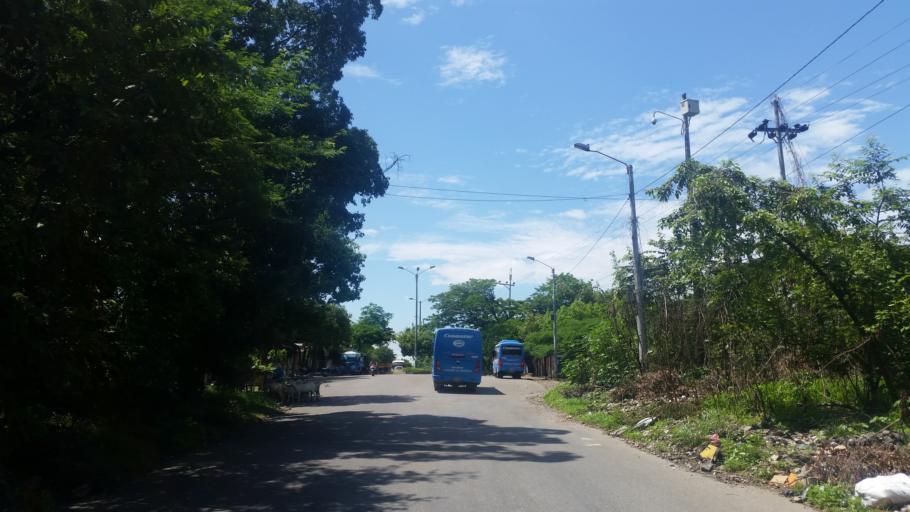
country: CO
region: Huila
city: Neiva
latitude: 2.9805
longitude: -75.2834
